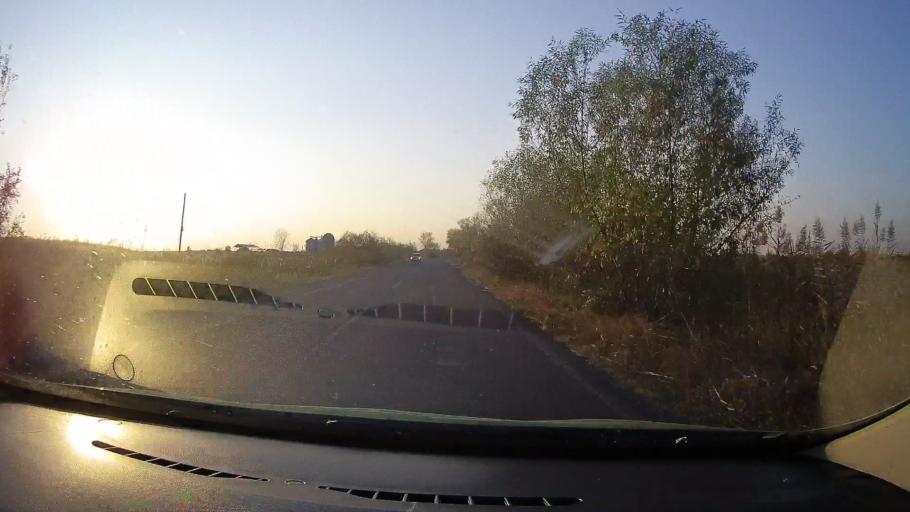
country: RO
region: Arad
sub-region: Comuna Bocsig
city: Bocsig
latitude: 46.4207
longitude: 21.9249
